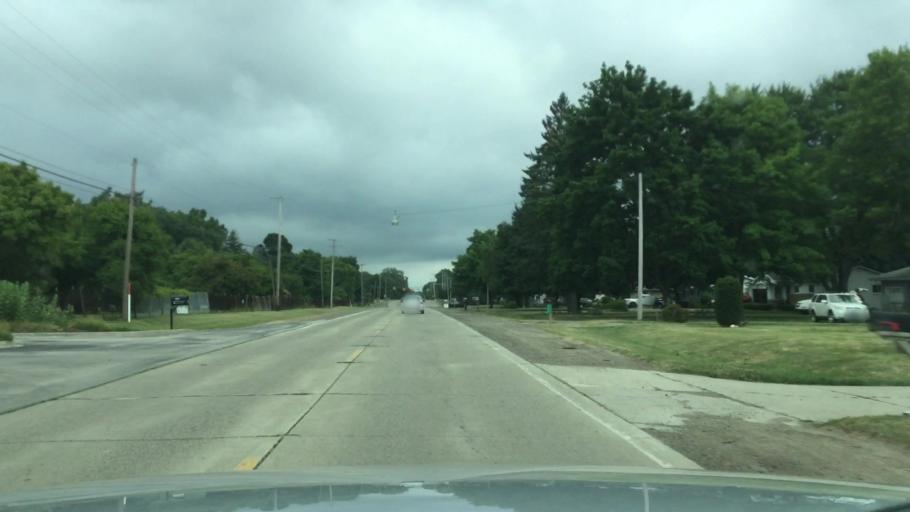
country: US
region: Michigan
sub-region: Genesee County
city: Burton
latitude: 43.0370
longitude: -83.6156
